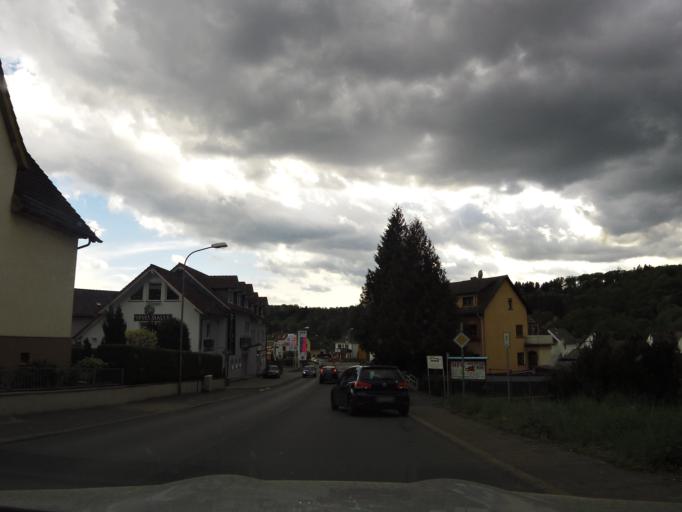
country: DE
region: Hesse
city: Solms
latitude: 50.5308
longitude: 8.4120
